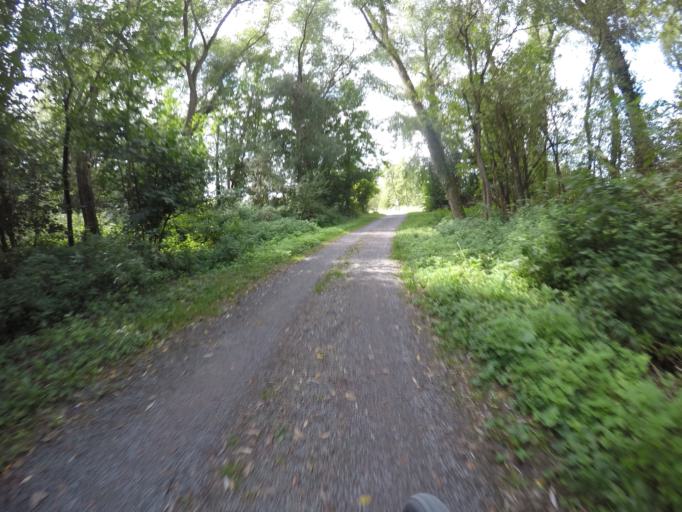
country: DE
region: Baden-Wuerttemberg
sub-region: Karlsruhe Region
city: Ubstadt-Weiher
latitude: 49.1751
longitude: 8.6381
